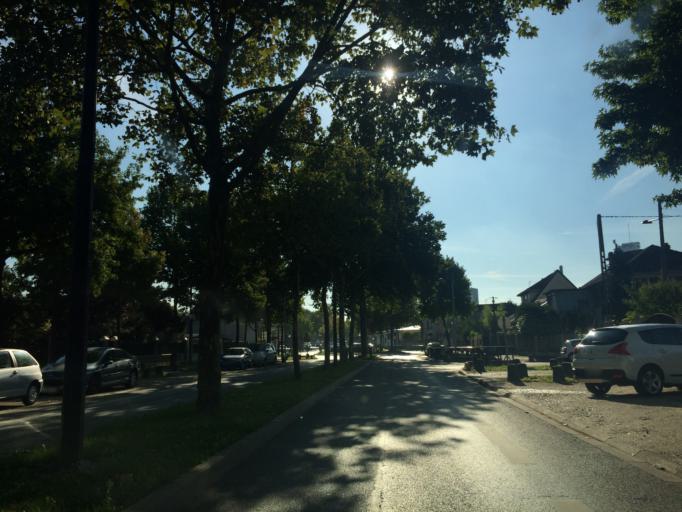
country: FR
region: Ile-de-France
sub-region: Departement du Val-de-Marne
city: Chennevieres-sur-Marne
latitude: 48.8098
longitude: 2.5433
